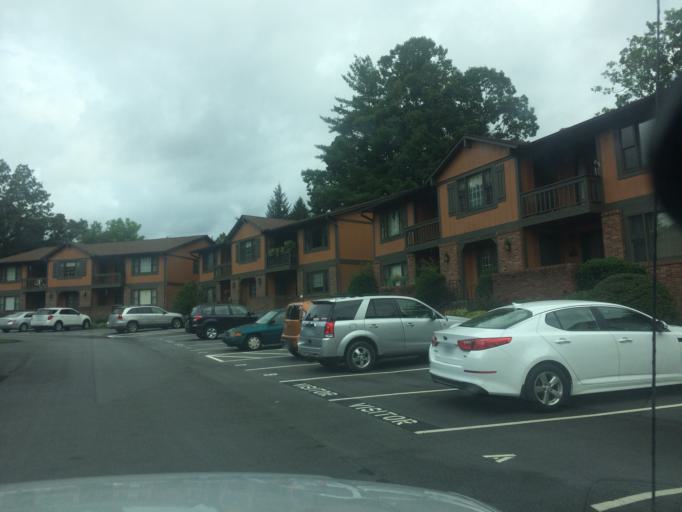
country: US
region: North Carolina
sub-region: Henderson County
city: Hendersonville
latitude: 35.3284
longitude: -82.4747
